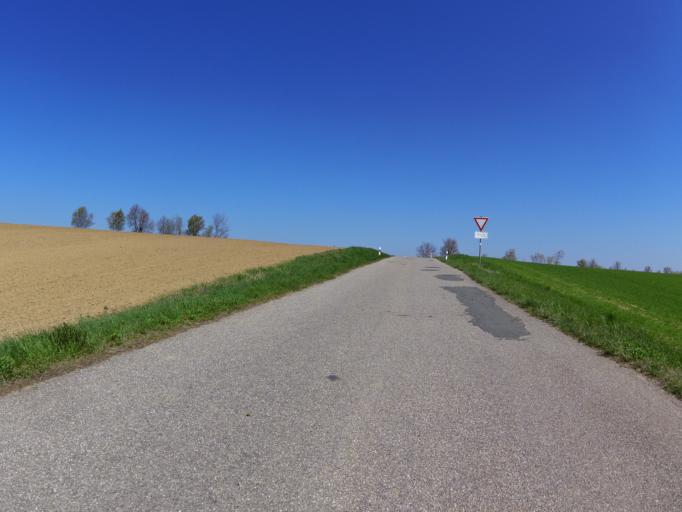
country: DE
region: Bavaria
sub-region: Regierungsbezirk Unterfranken
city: Biebelried
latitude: 49.7838
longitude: 10.0769
